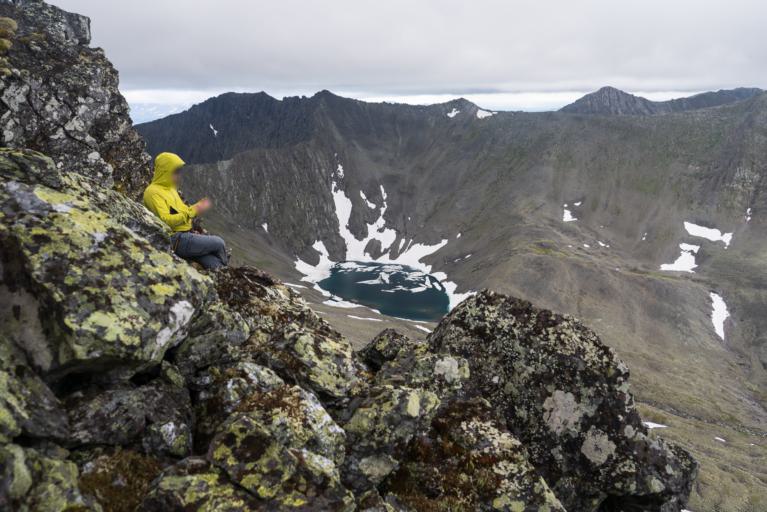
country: RU
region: Komi Republic
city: Synya
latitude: 64.8134
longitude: 59.2225
